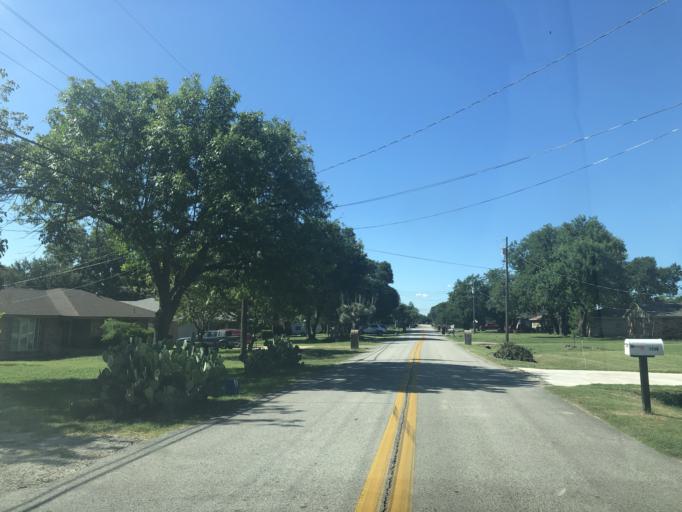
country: US
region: Texas
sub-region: Dallas County
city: Duncanville
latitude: 32.6526
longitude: -96.9355
